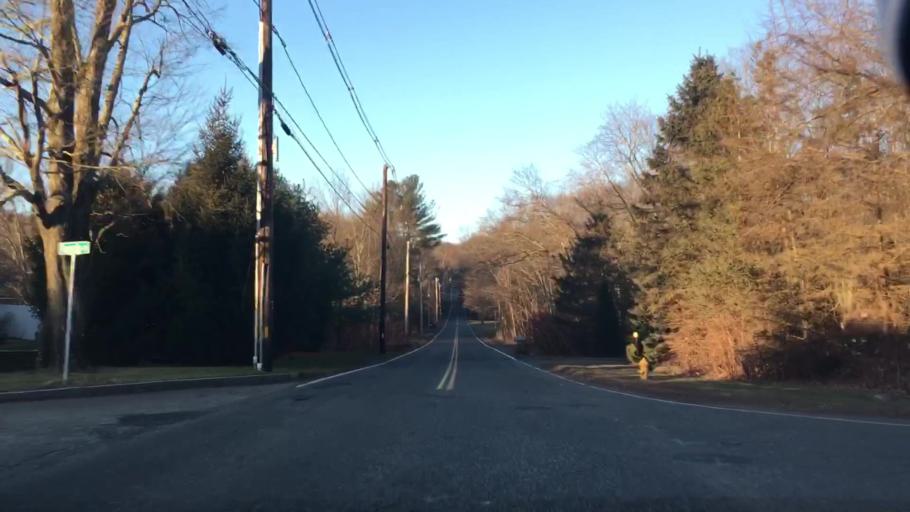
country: US
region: Massachusetts
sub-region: Hampden County
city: East Longmeadow
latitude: 42.0444
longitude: -72.4920
